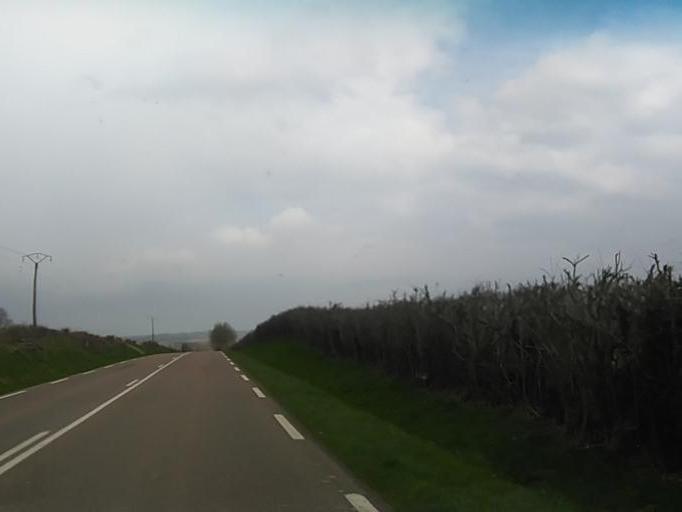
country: FR
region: Lower Normandy
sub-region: Departement de l'Orne
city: Pont-Ecrepin
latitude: 48.7285
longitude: -0.2577
